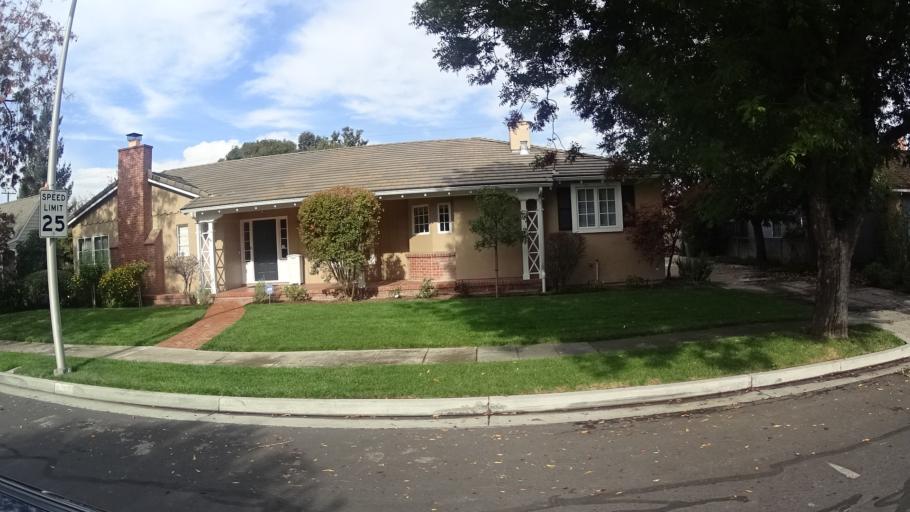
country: US
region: California
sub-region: Santa Clara County
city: Burbank
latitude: 37.3417
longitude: -121.9356
